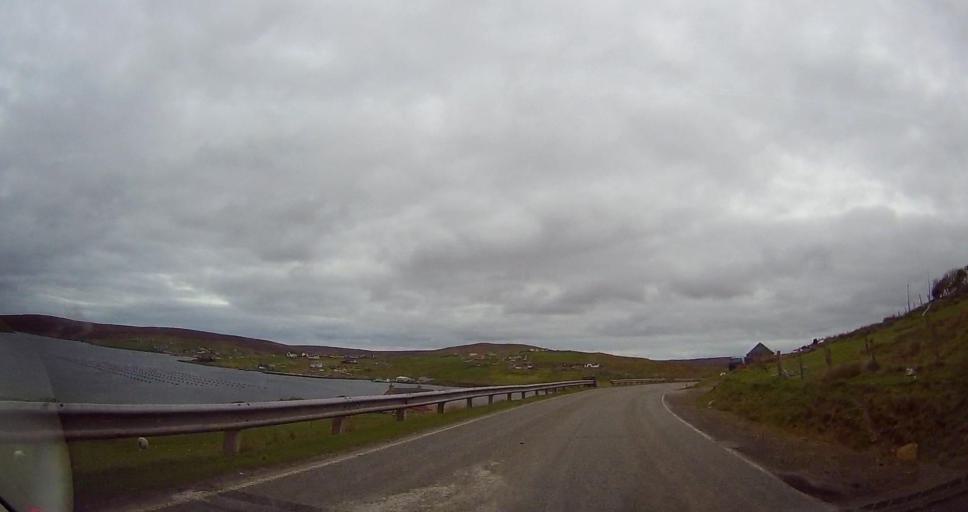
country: GB
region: Scotland
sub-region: Shetland Islands
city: Shetland
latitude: 60.6116
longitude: -1.0736
